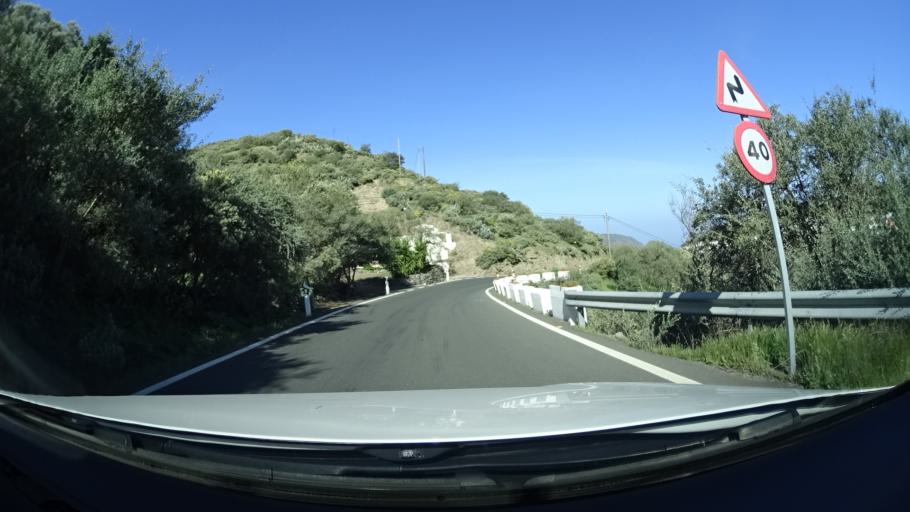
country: ES
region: Canary Islands
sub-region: Provincia de Las Palmas
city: Artenara
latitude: 28.0246
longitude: -15.6381
